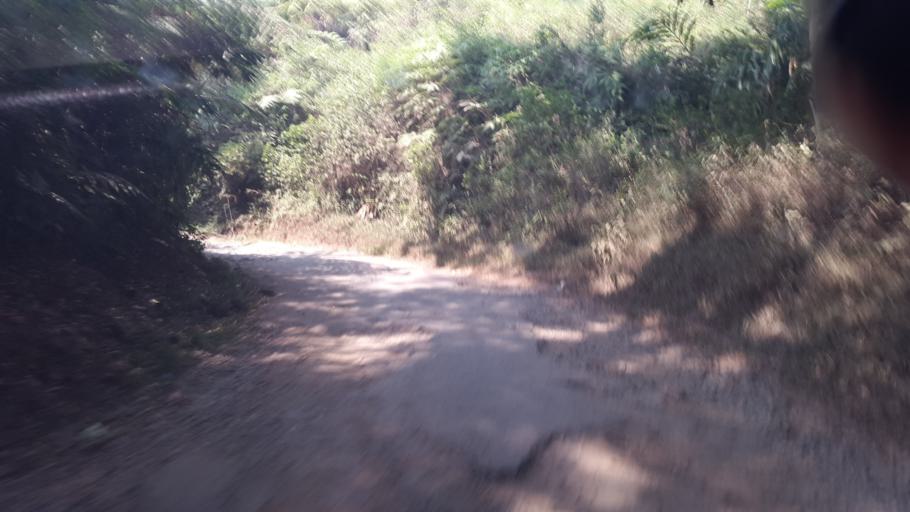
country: ID
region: West Java
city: Pasirreungit
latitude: -6.9995
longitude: 107.0049
